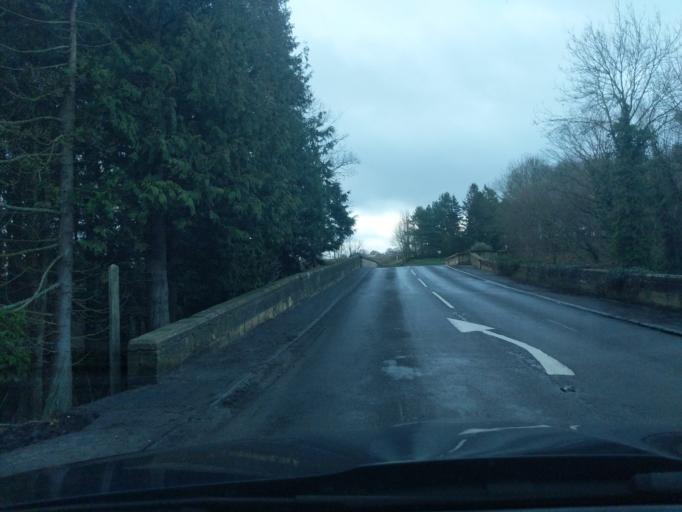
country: GB
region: England
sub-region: Northumberland
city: Alnwick
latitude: 55.4183
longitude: -1.6897
